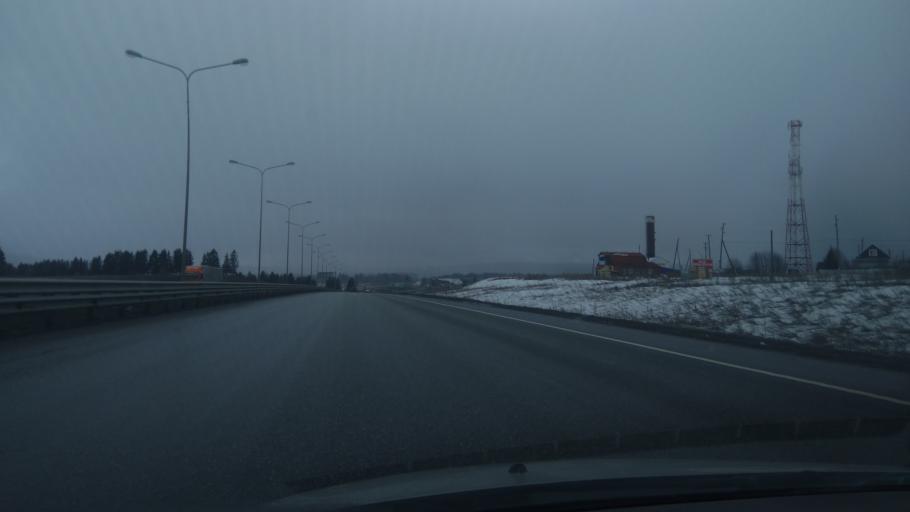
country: RU
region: Perm
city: Zvezdnyy
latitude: 57.7917
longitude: 56.3355
